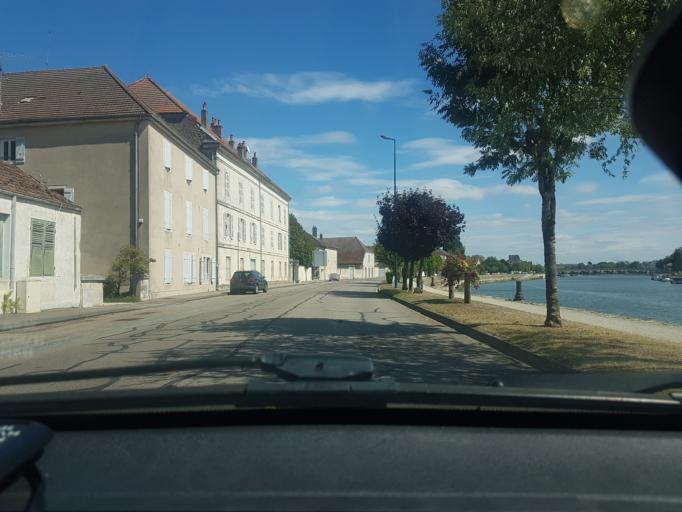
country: FR
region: Franche-Comte
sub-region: Departement de la Haute-Saone
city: Arc-les-Gray
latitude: 47.4507
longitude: 5.5806
